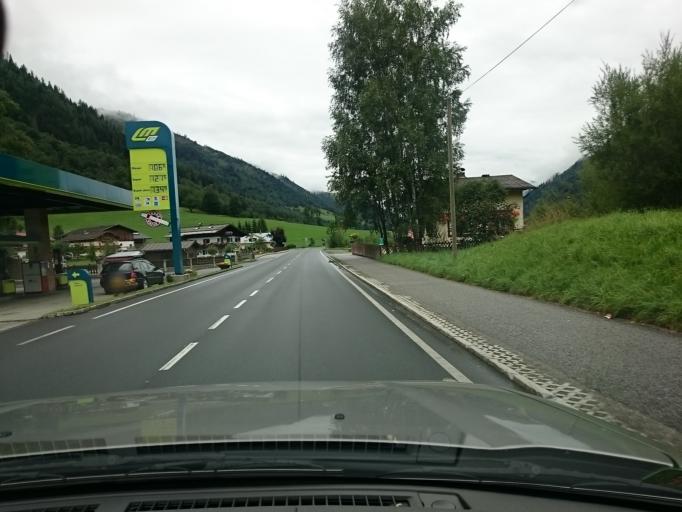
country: AT
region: Salzburg
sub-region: Politischer Bezirk Zell am See
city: Bruck an der Grossglocknerstrasse
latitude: 47.2317
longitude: 12.8256
